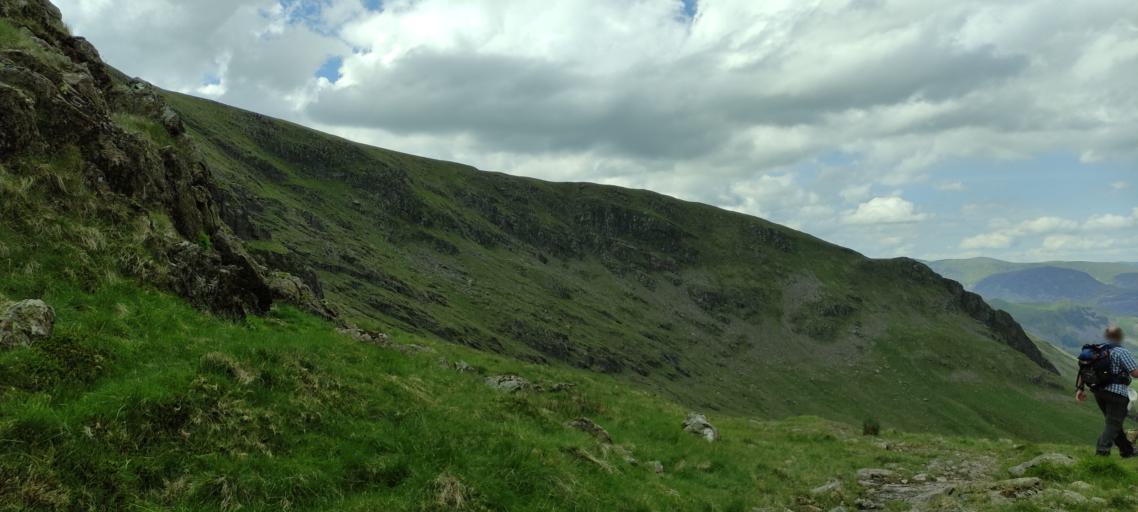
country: GB
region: England
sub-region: Cumbria
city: Ambleside
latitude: 54.4853
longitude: -2.8870
